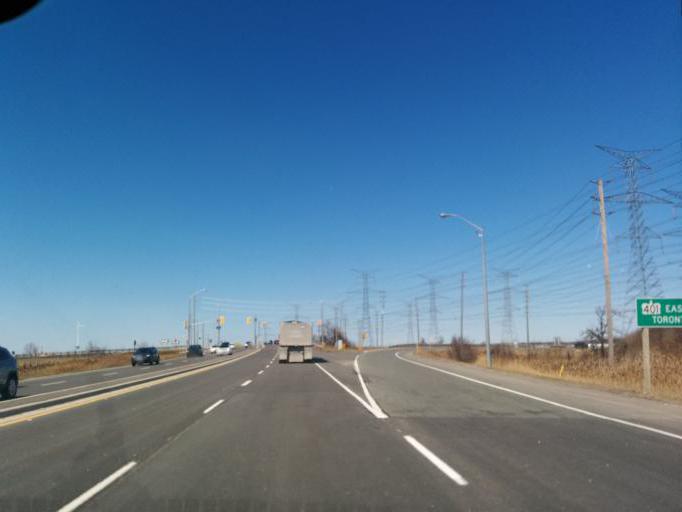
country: CA
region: Ontario
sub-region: Halton
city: Milton
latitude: 43.5402
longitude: -79.8596
